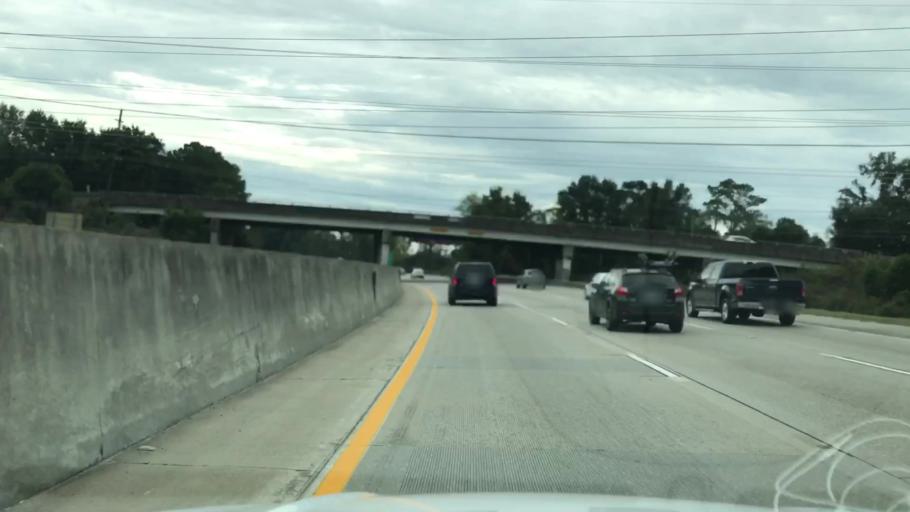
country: US
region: South Carolina
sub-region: Charleston County
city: North Charleston
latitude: 32.8480
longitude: -79.9873
